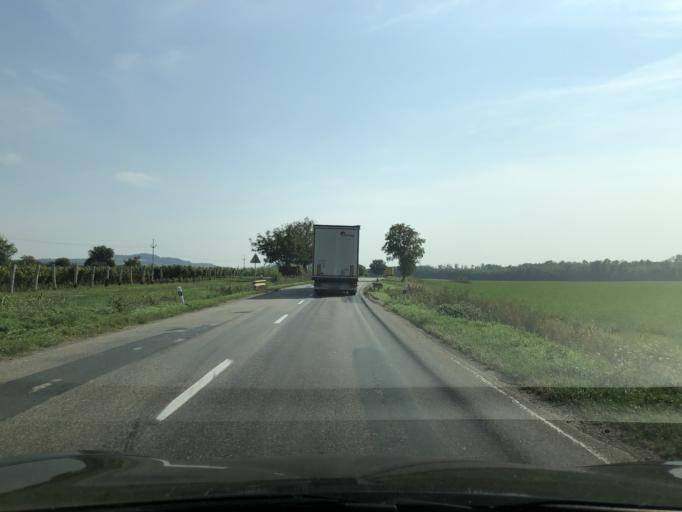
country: CZ
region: South Moravian
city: Brezi
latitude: 48.8198
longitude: 16.5810
